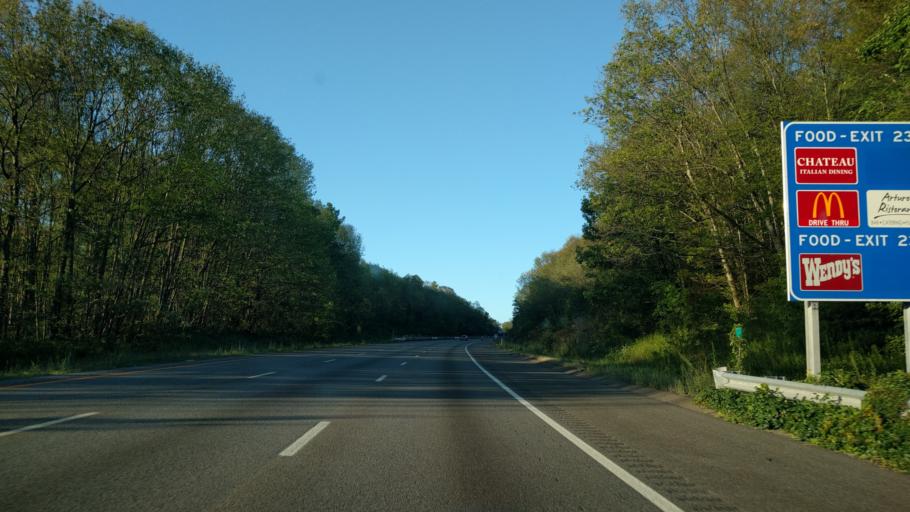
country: US
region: Massachusetts
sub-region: Worcester County
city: Southborough
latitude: 42.3021
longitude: -71.5655
